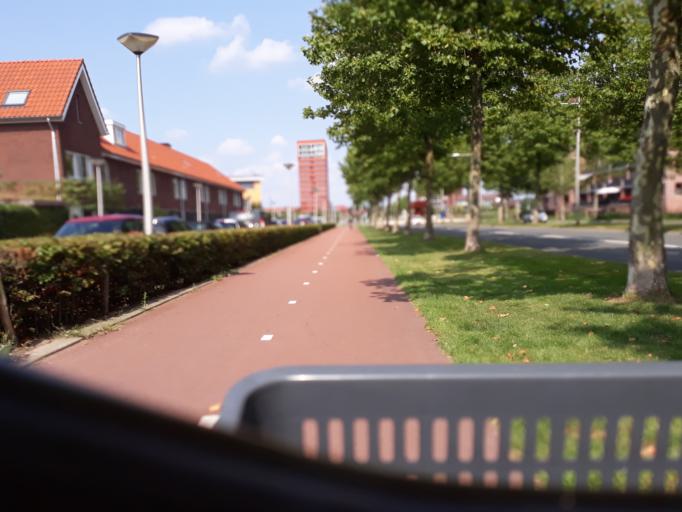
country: NL
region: South Holland
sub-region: Gemeente Hendrik-Ido-Ambacht
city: Hendrik-Ido-Ambacht
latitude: 51.8320
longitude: 4.6507
